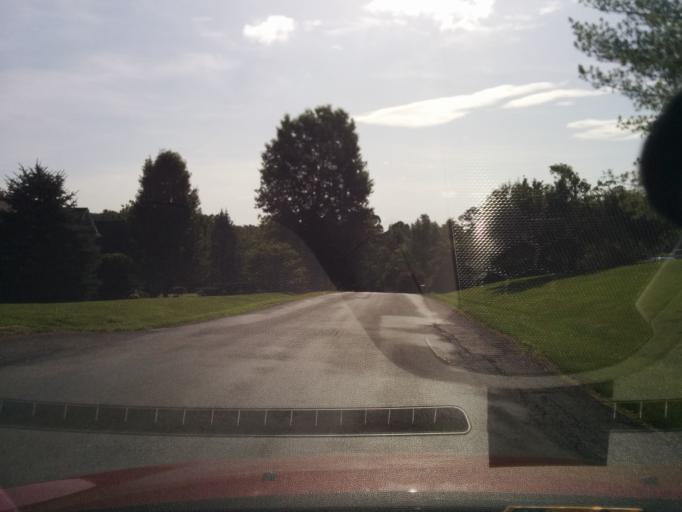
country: US
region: Virginia
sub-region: City of Lexington
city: Lexington
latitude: 37.7679
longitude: -79.4613
